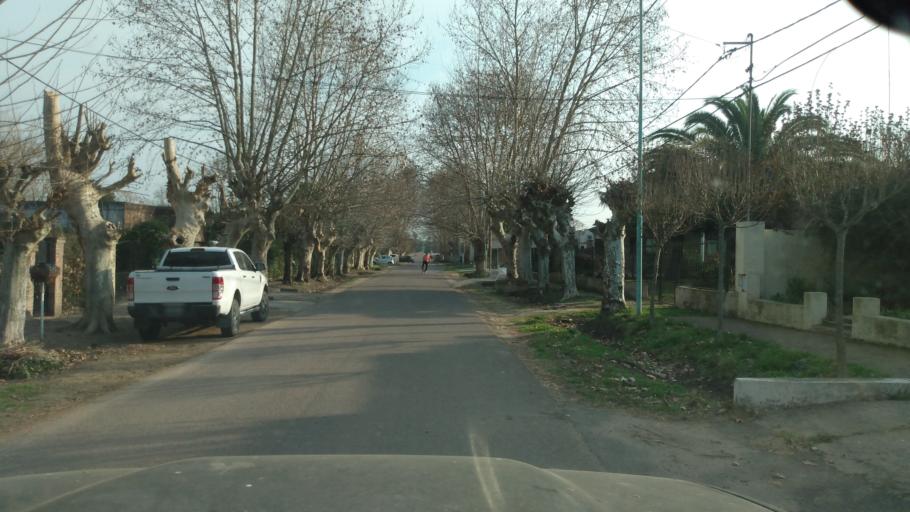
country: AR
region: Buenos Aires
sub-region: Partido de Lujan
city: Lujan
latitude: -34.5798
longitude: -59.1764
